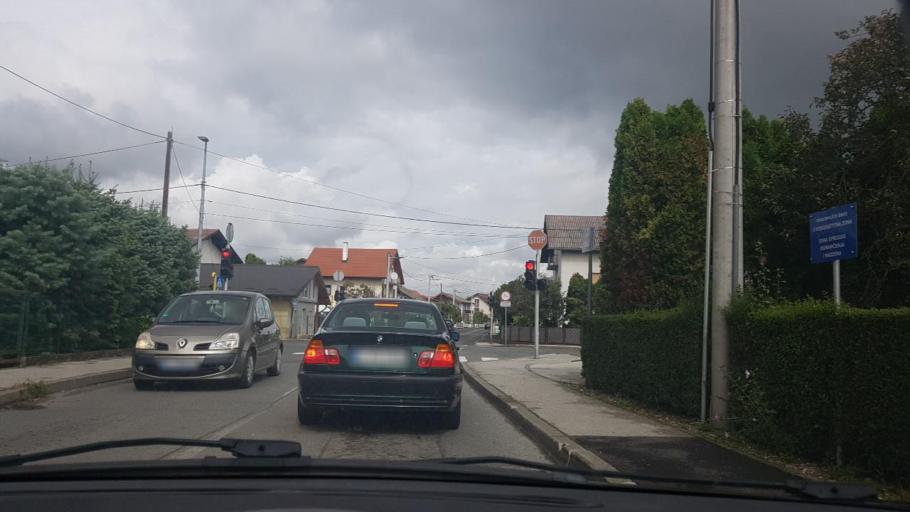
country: HR
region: Zagrebacka
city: Brdovec
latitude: 45.8622
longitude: 15.7906
